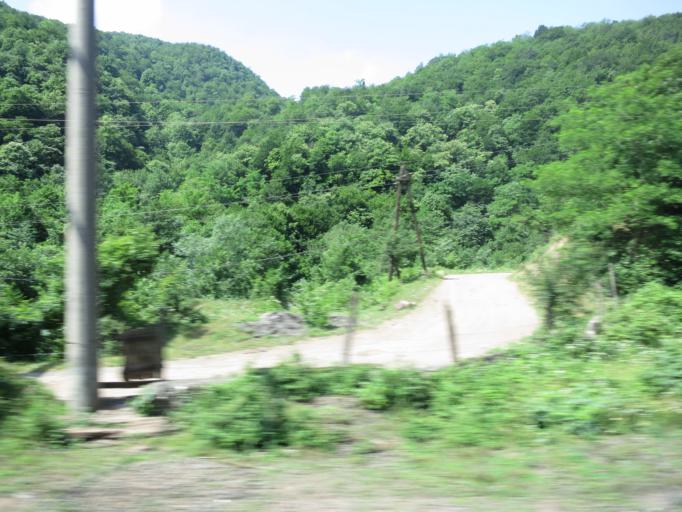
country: GE
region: Imereti
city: Kharagauli
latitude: 42.0015
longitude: 43.2238
